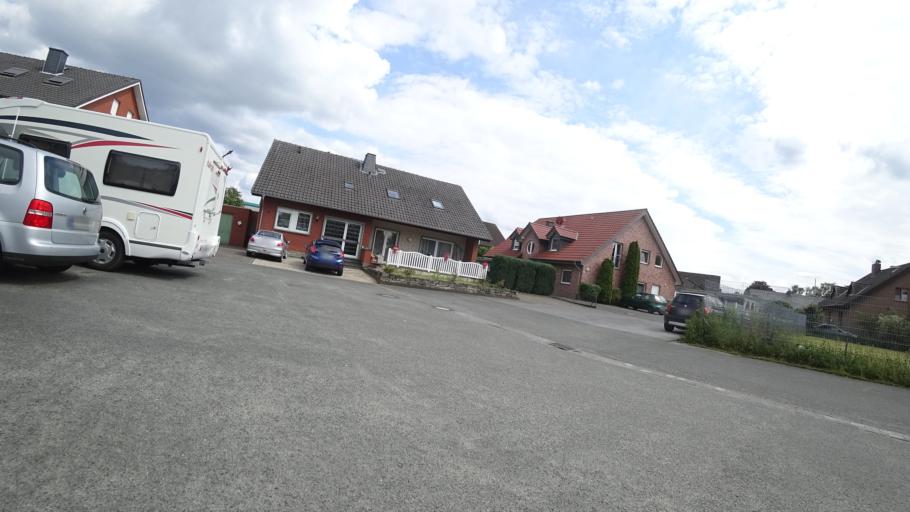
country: DE
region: North Rhine-Westphalia
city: Rietberg
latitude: 51.8158
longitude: 8.4237
